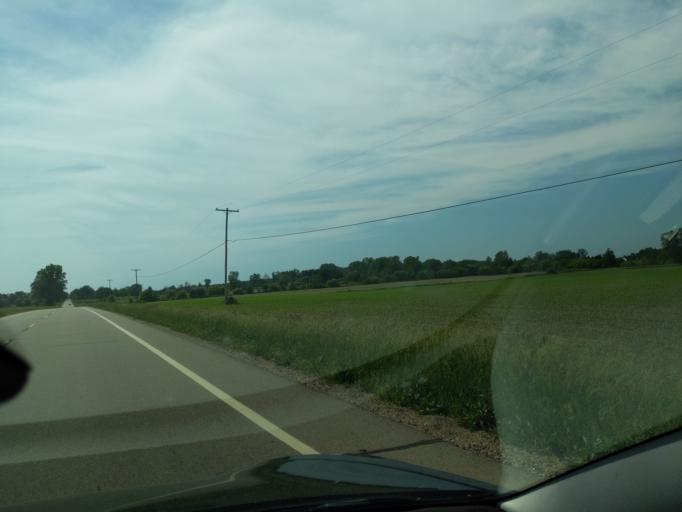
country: US
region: Michigan
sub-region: Eaton County
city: Grand Ledge
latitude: 42.7120
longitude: -84.8105
